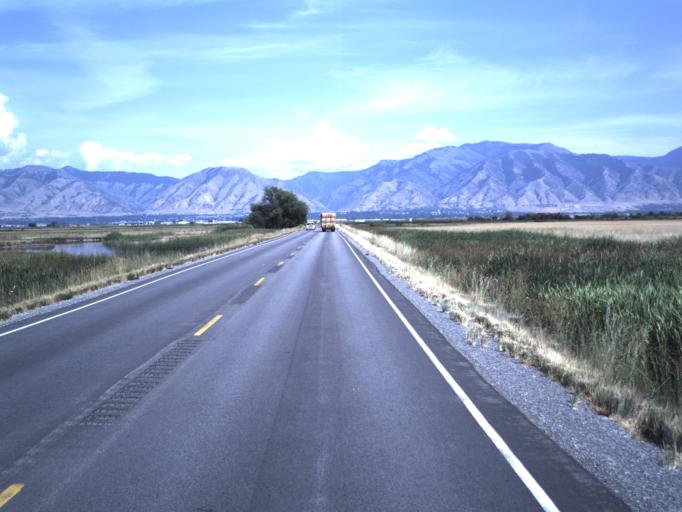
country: US
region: Utah
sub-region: Cache County
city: Benson
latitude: 41.7459
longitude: -111.9393
